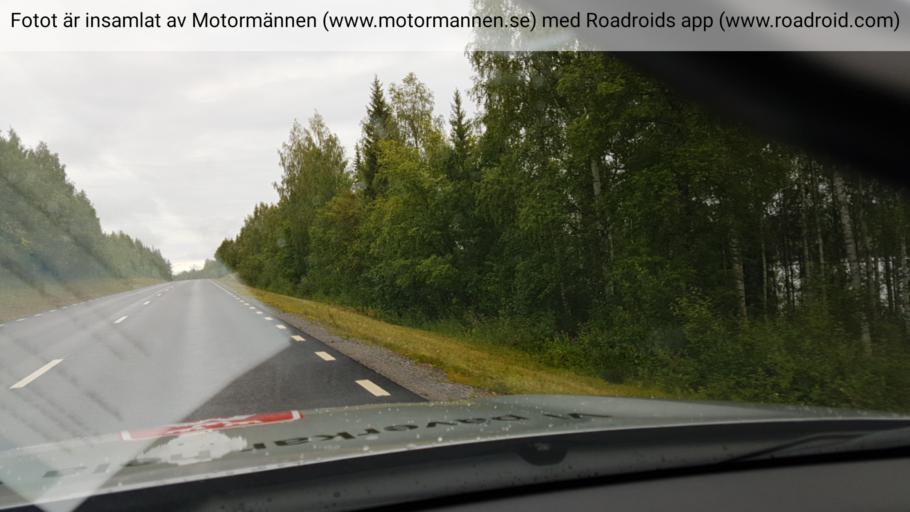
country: SE
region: Norrbotten
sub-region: Alvsbyns Kommun
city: AElvsbyn
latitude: 66.2659
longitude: 20.8327
